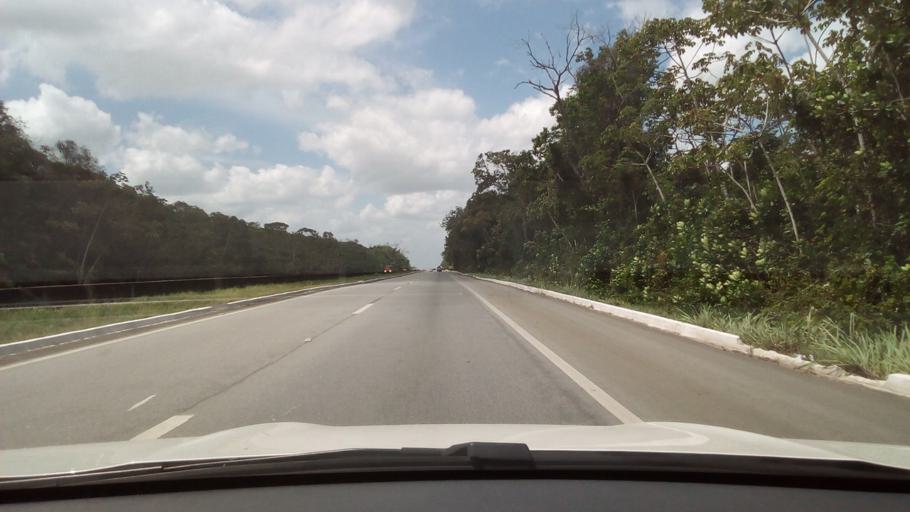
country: BR
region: Paraiba
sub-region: Mamanguape
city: Mamanguape
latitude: -6.9753
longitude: -35.0790
